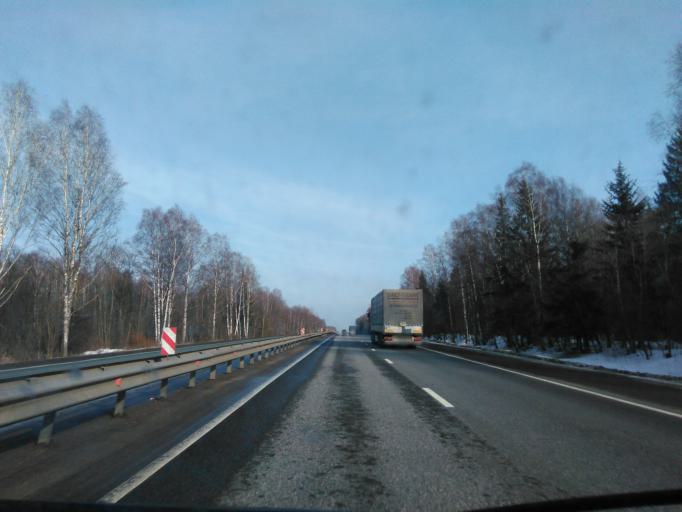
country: RU
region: Smolensk
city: Kholm-Zhirkovskiy
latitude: 55.1910
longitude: 33.7784
